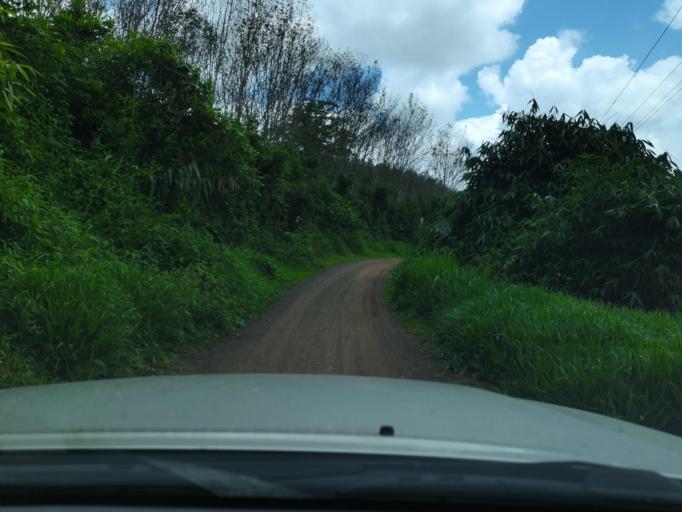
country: LA
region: Loungnamtha
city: Muang Long
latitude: 20.7519
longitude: 101.0182
